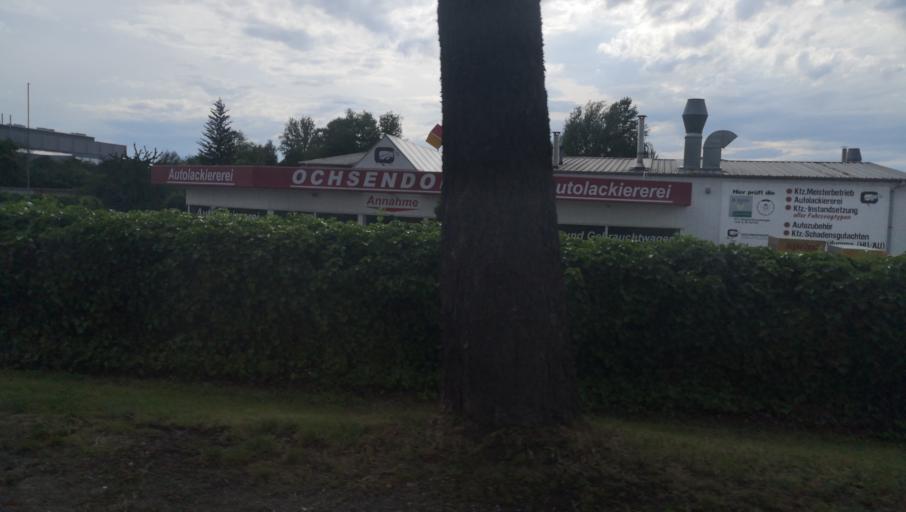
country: DE
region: Saxony-Anhalt
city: Barleben
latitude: 52.1923
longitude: 11.6233
